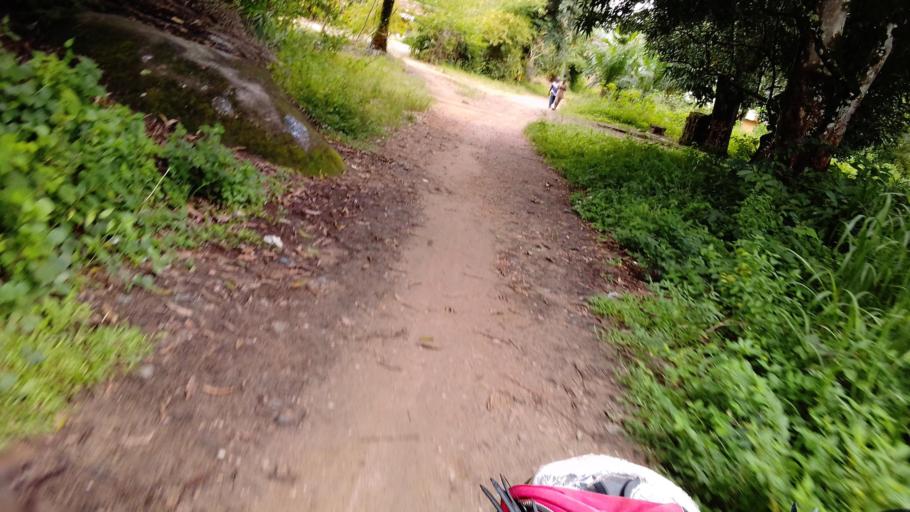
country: SL
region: Eastern Province
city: Koidu
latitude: 8.6767
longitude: -10.9868
